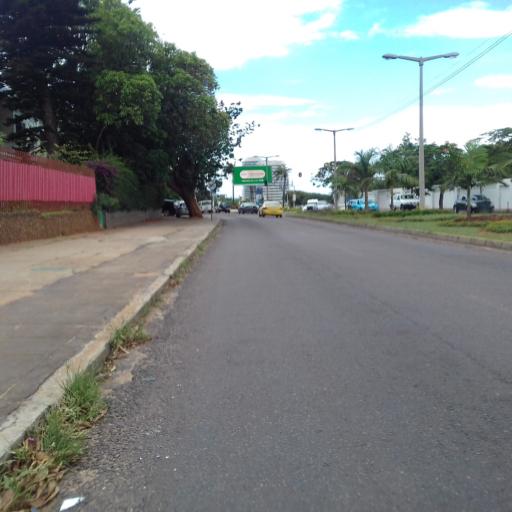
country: MZ
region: Maputo City
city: Maputo
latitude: -25.9619
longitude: 32.6016
